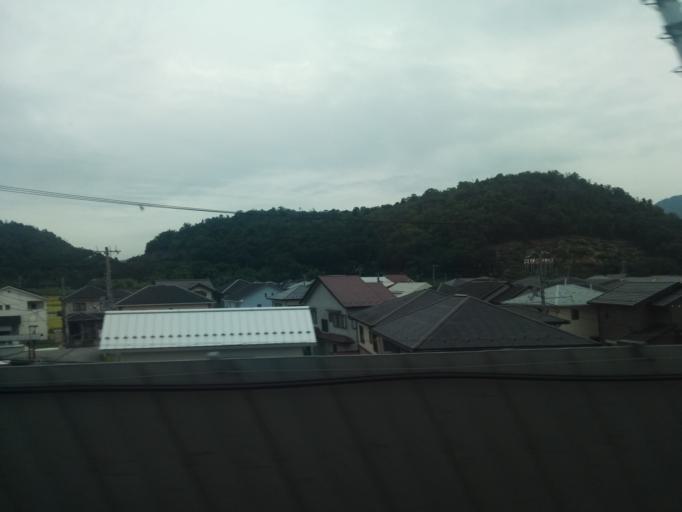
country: JP
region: Shiga Prefecture
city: Nagahama
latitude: 35.3257
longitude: 136.2922
